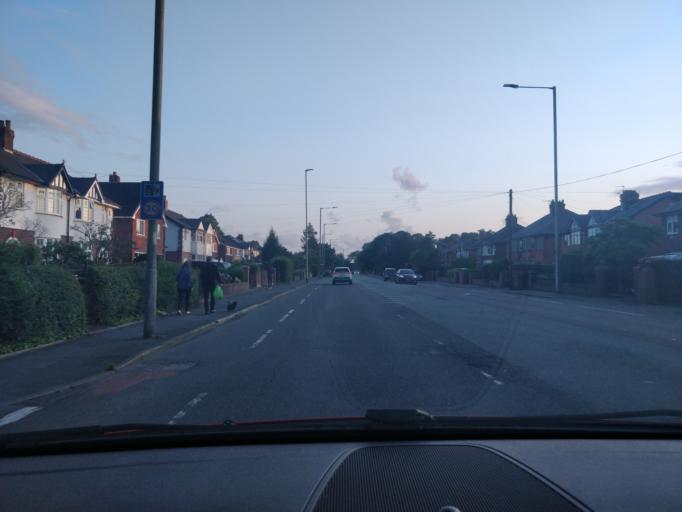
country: GB
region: England
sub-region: Lancashire
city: Preston
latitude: 53.7463
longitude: -2.7395
